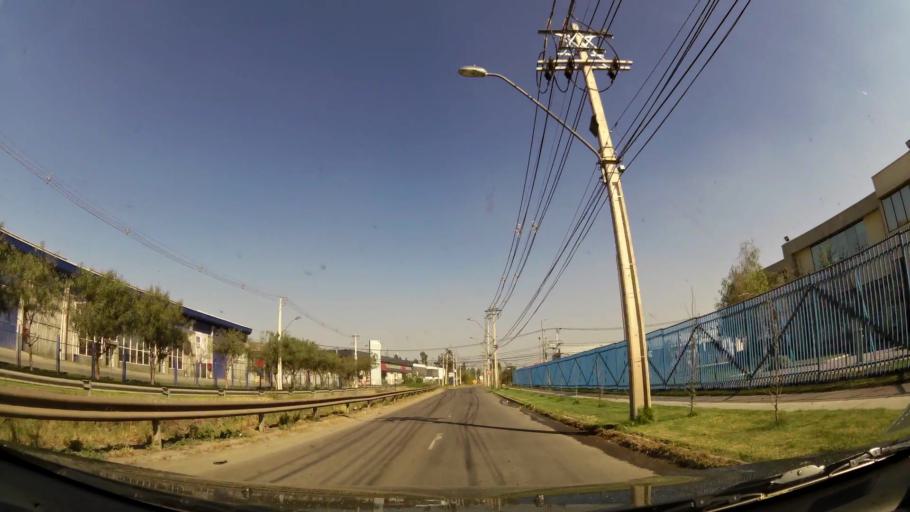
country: CL
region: Santiago Metropolitan
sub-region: Provincia de Chacabuco
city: Chicureo Abajo
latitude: -33.3412
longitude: -70.7014
